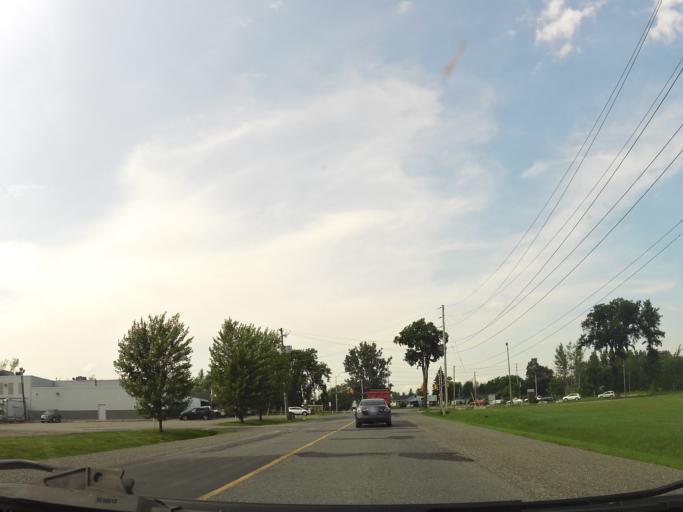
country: CA
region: Ontario
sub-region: Lanark County
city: Smiths Falls
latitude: 44.9049
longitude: -76.0313
